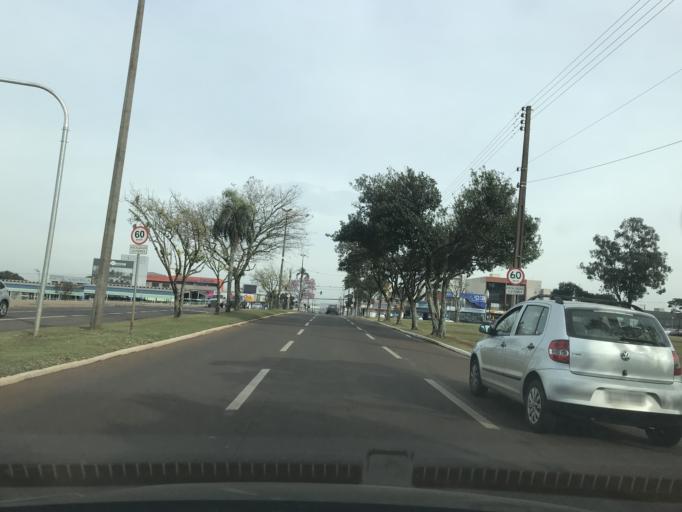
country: BR
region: Parana
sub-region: Cascavel
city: Cascavel
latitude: -24.9542
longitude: -53.4787
